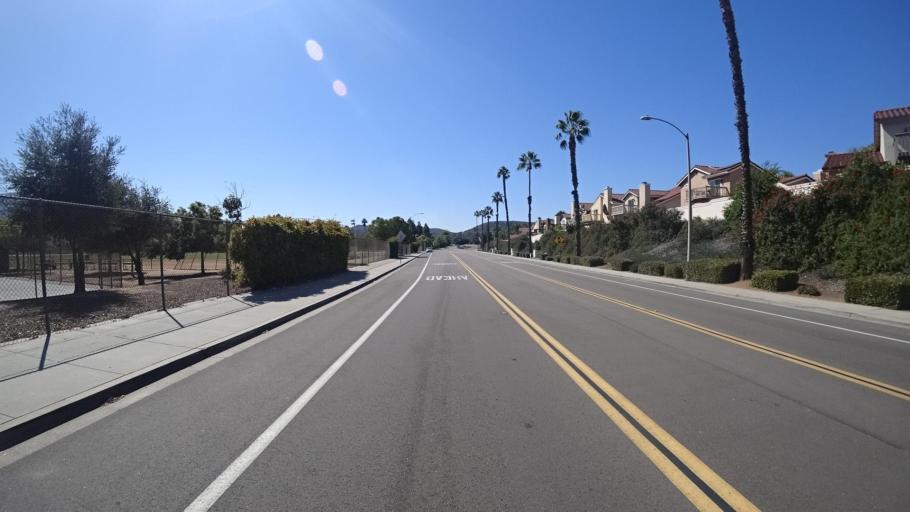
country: US
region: California
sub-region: San Diego County
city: Rancho San Diego
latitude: 32.7483
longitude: -116.9352
